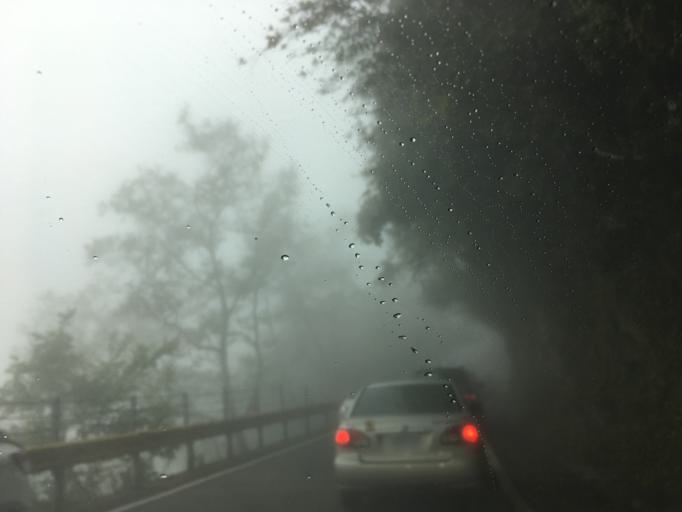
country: TW
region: Taiwan
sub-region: Hualien
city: Hualian
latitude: 24.1867
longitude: 121.4221
